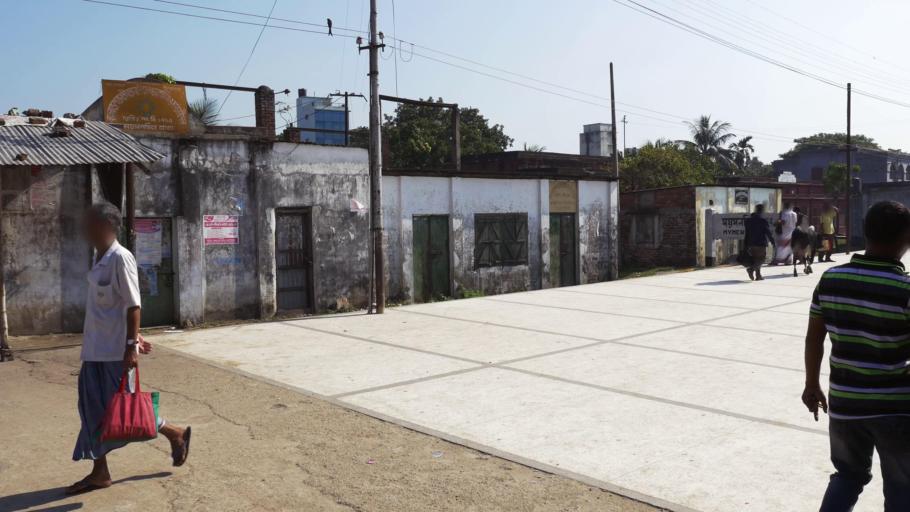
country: BD
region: Dhaka
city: Mymensingh
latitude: 24.6855
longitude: 90.4546
